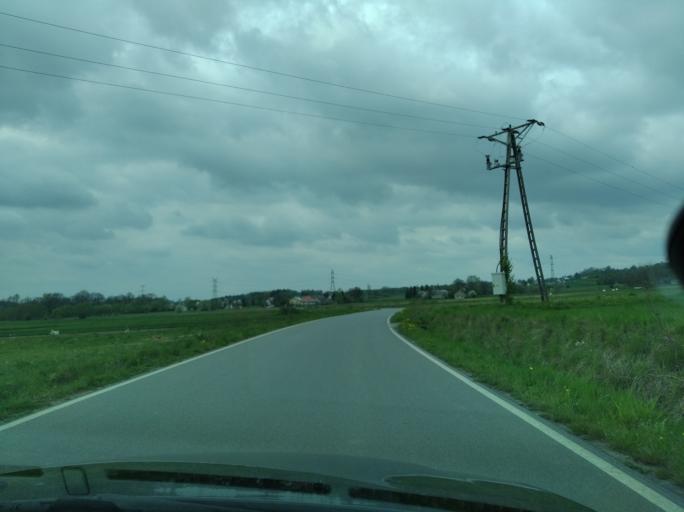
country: PL
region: Subcarpathian Voivodeship
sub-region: Powiat brzozowski
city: Jablonica Polska
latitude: 49.6994
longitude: 21.8881
